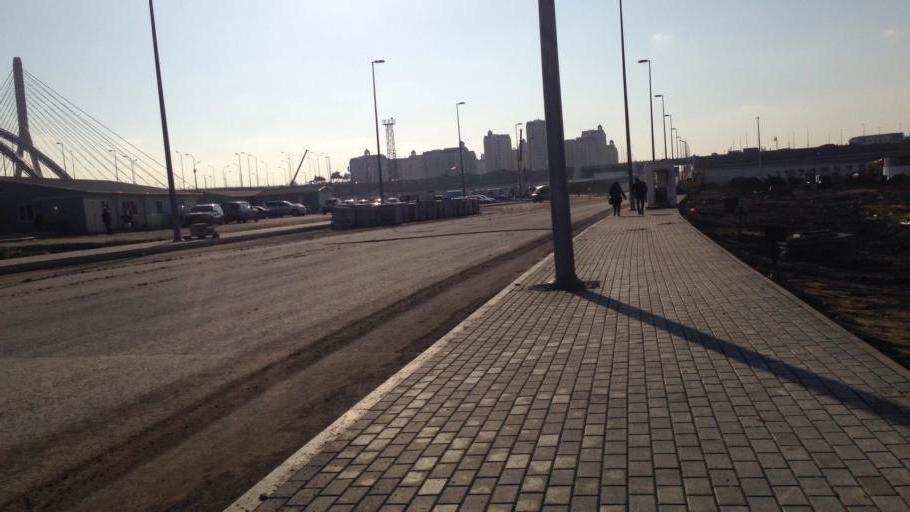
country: AZ
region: Baki
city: Sabuncu
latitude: 40.4276
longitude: 49.9224
